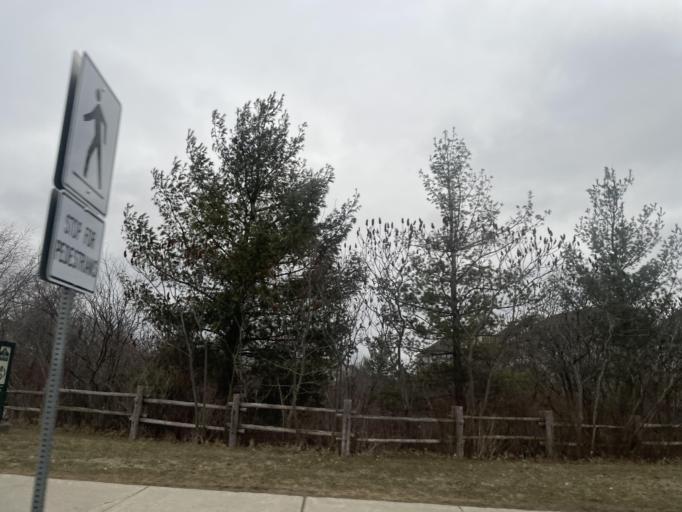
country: CA
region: Ontario
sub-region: Wellington County
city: Guelph
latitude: 43.5042
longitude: -80.1904
